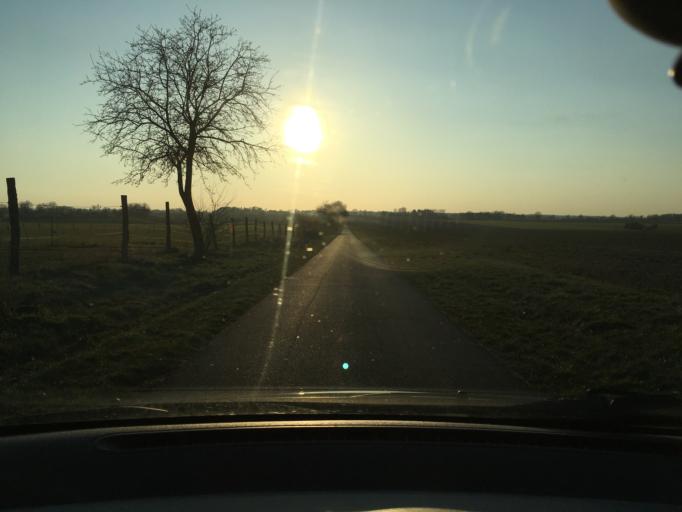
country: DE
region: Lower Saxony
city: Romstedt
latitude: 53.1484
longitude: 10.6594
